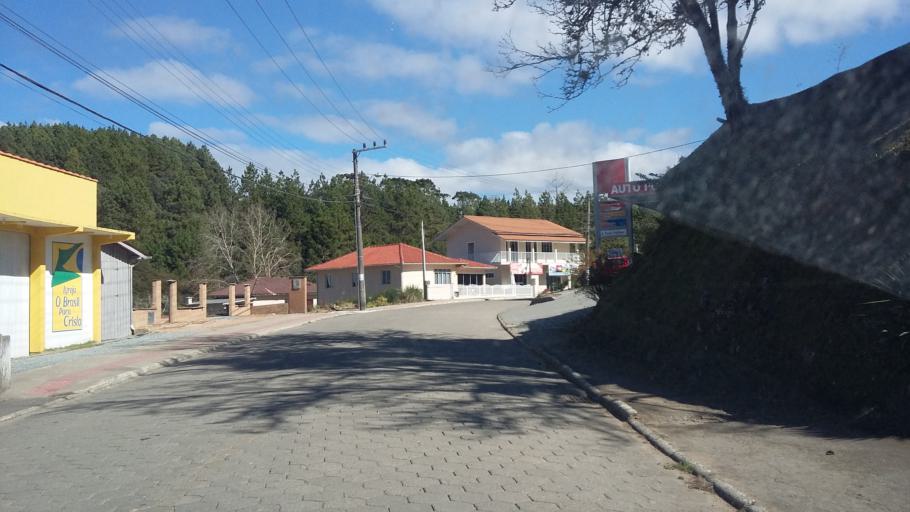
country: BR
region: Santa Catarina
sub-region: Santo Amaro Da Imperatriz
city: Santo Amaro da Imperatriz
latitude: -27.6774
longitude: -49.0089
